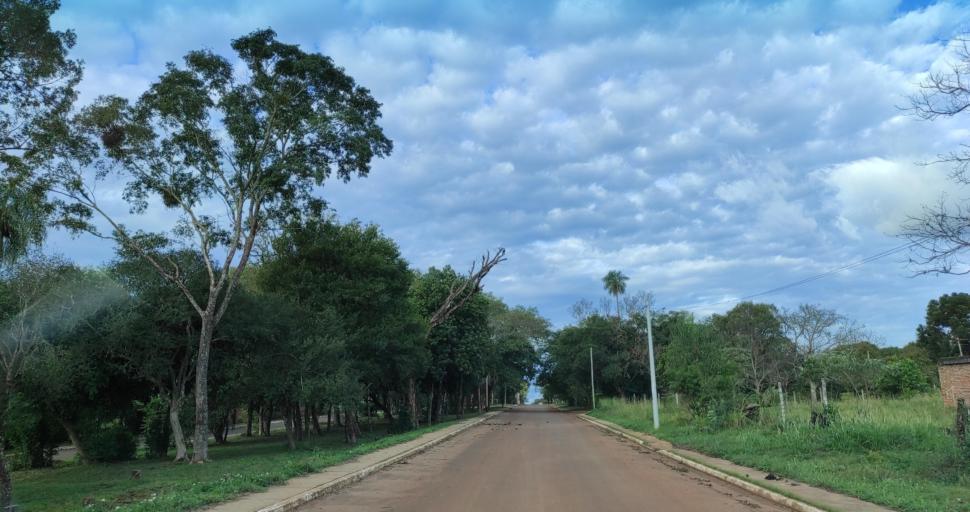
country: AR
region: Misiones
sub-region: Departamento de Candelaria
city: Candelaria
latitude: -27.4519
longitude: -55.7521
